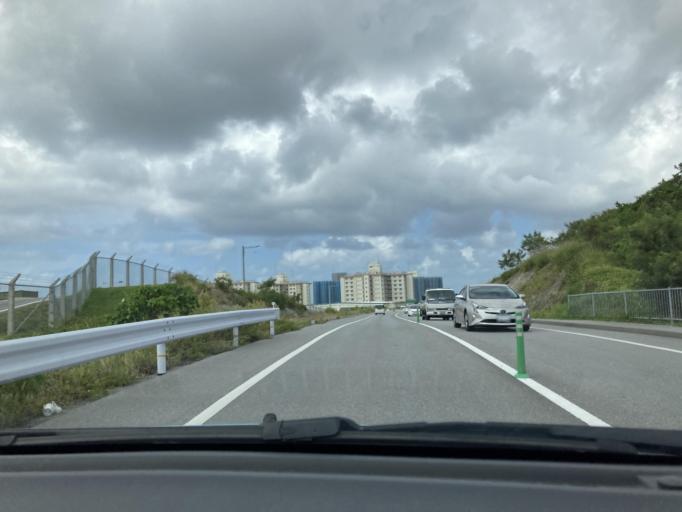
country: JP
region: Okinawa
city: Ginowan
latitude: 26.2629
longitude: 127.7086
